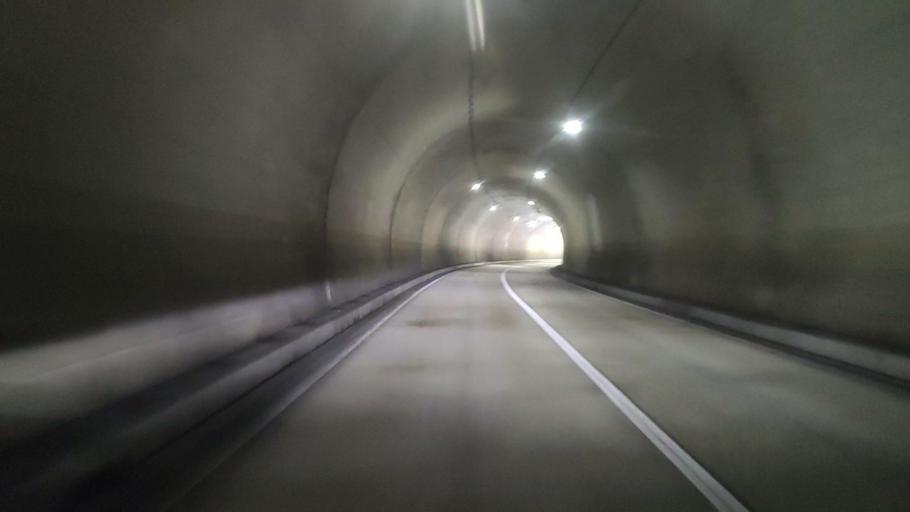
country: JP
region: Wakayama
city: Shingu
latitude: 33.8725
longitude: 135.8559
